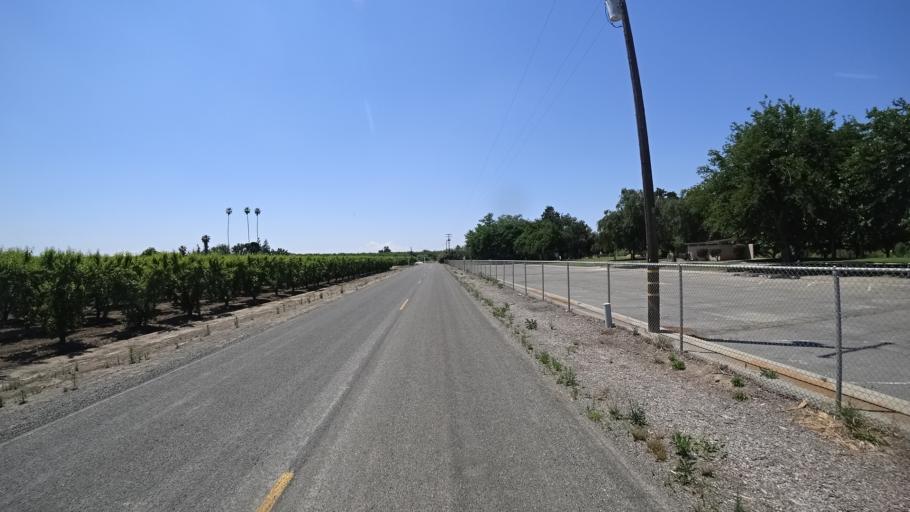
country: US
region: California
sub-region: Fresno County
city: Laton
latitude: 36.4230
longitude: -119.6922
